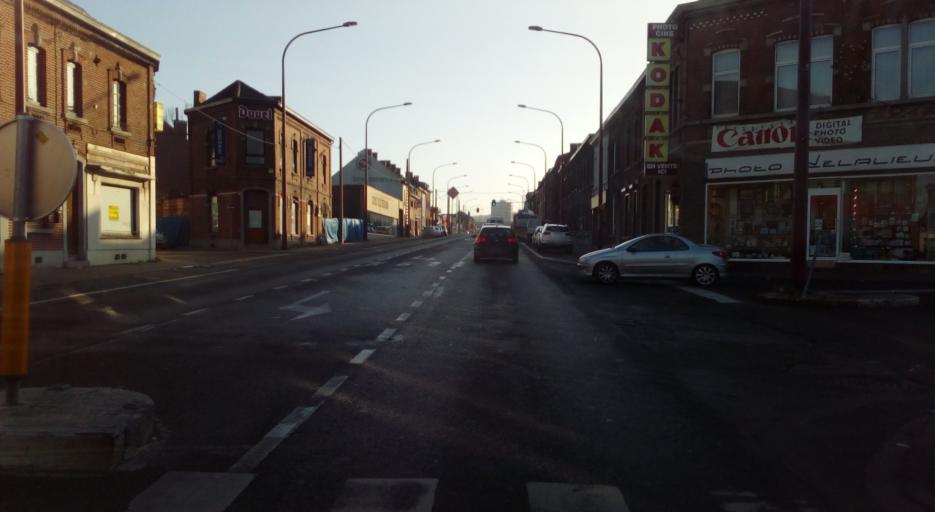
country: BE
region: Wallonia
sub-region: Province du Hainaut
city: Charleroi
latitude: 50.3889
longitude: 4.4608
